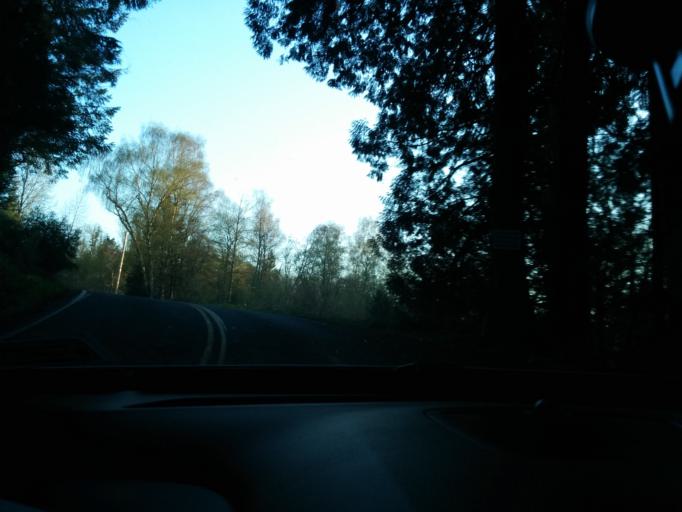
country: US
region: Washington
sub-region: Snohomish County
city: Sultan
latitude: 47.9015
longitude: -121.7843
